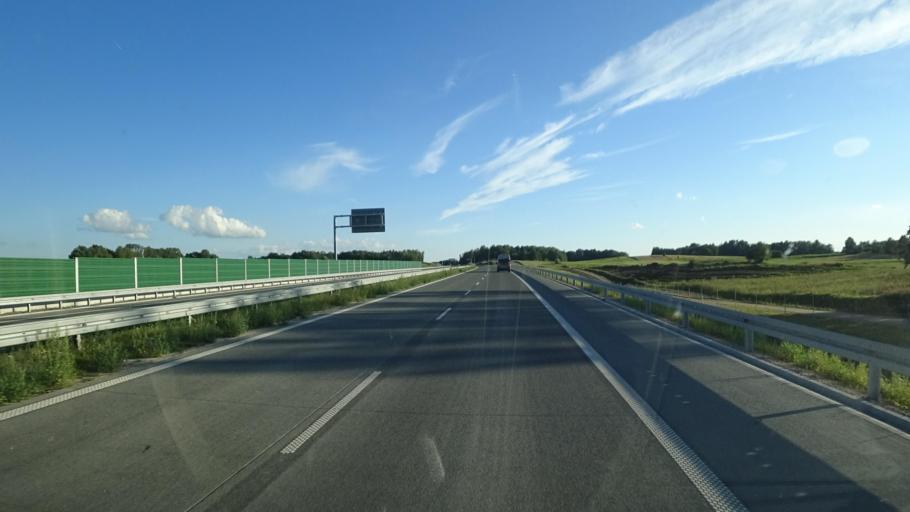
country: PL
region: Podlasie
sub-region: Powiat suwalski
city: Raczki
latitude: 53.9623
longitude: 22.7751
